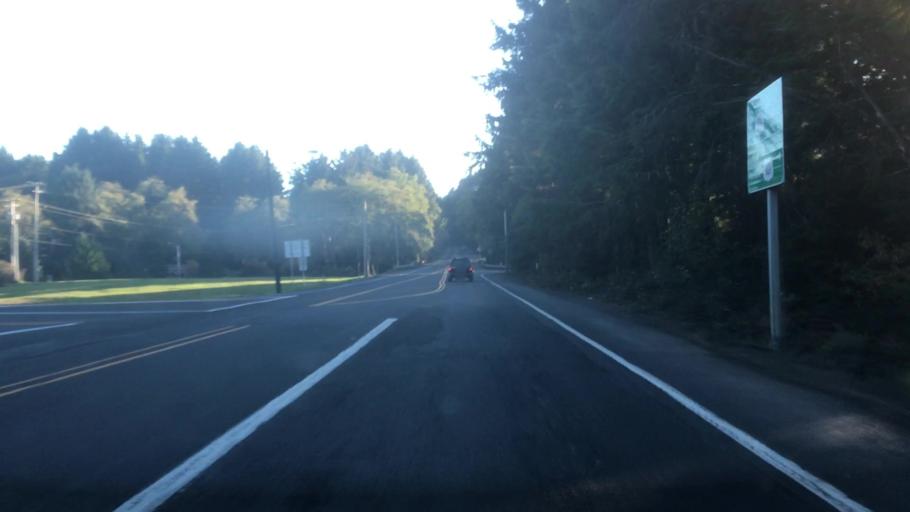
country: US
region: Oregon
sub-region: Clatsop County
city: Cannon Beach
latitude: 45.8890
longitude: -123.9576
